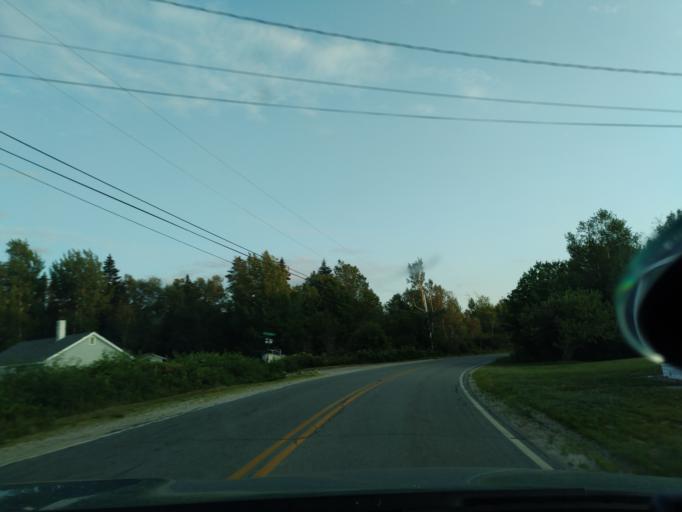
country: US
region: Maine
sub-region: Hancock County
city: Gouldsboro
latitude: 44.3714
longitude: -68.0338
